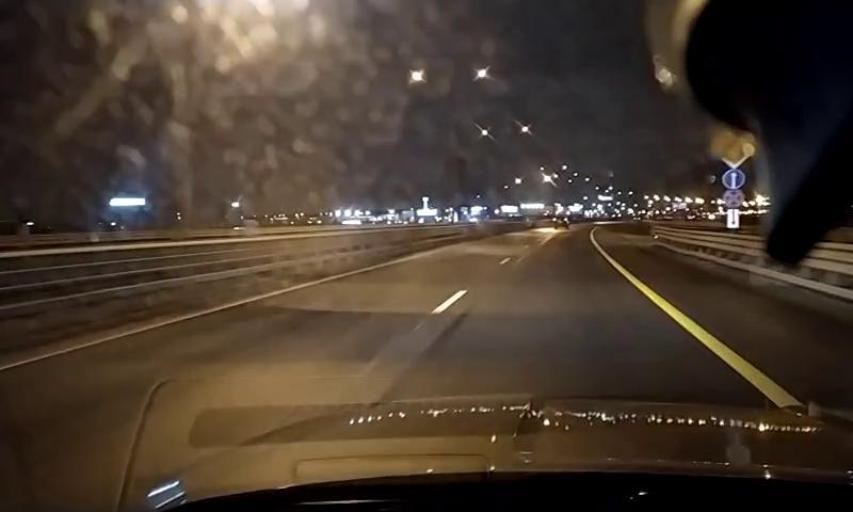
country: RU
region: Leningrad
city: Bugry
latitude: 60.0995
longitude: 30.3830
